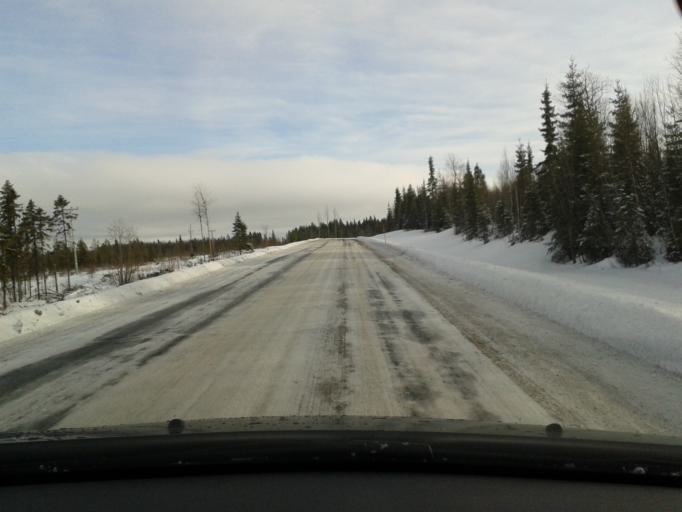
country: SE
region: Vaesterbotten
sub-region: Vilhelmina Kommun
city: Sjoberg
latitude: 64.7446
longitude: 16.1893
